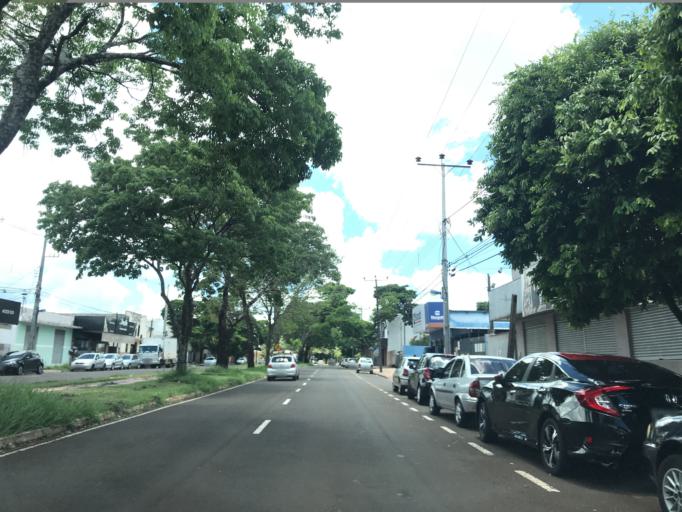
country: BR
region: Parana
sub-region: Maringa
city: Maringa
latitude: -23.3934
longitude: -51.9174
